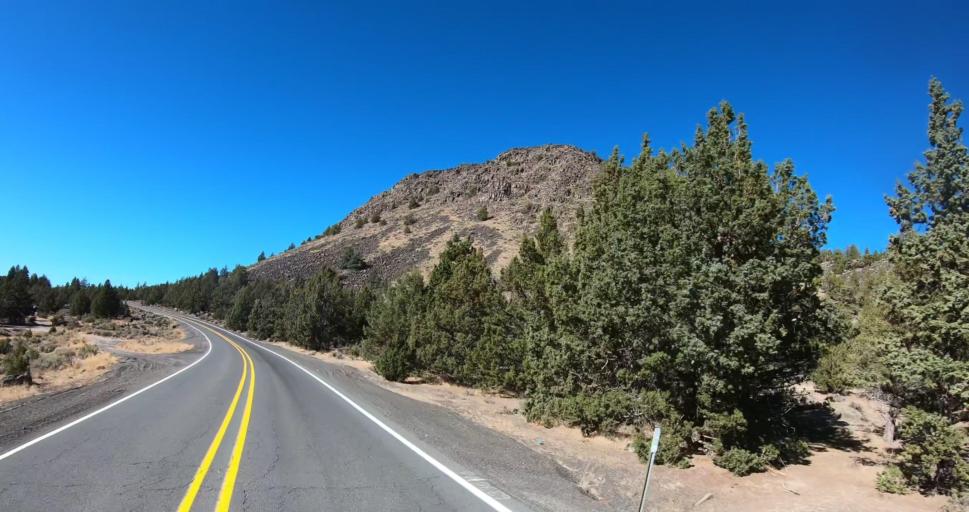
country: US
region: Oregon
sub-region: Deschutes County
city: La Pine
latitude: 43.0470
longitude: -120.7964
